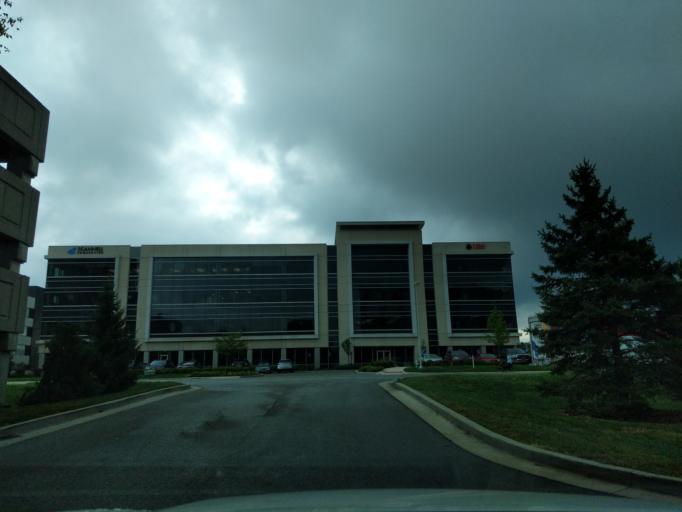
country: US
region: Indiana
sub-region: Marion County
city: Meridian Hills
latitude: 39.9156
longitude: -86.1071
